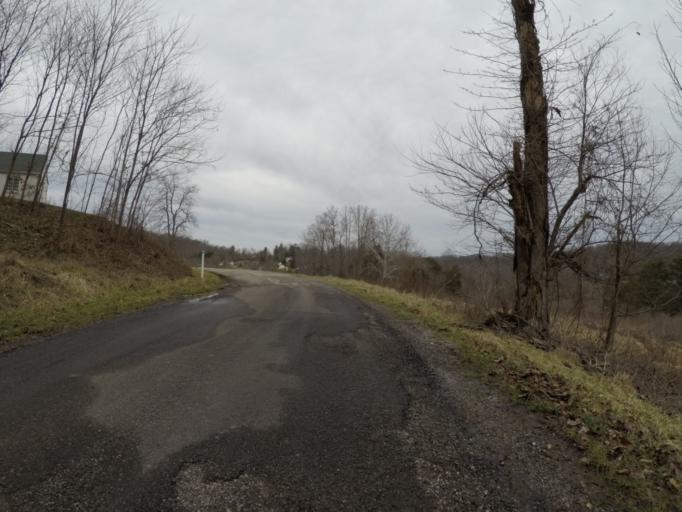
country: US
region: Ohio
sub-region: Lawrence County
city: Burlington
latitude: 38.3810
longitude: -82.5126
